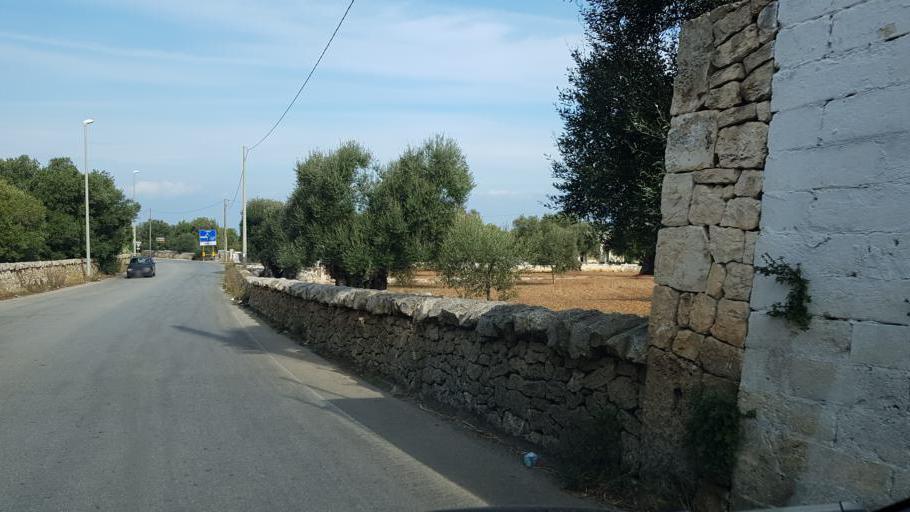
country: IT
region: Apulia
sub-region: Provincia di Brindisi
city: Ostuni
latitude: 40.7376
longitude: 17.5794
